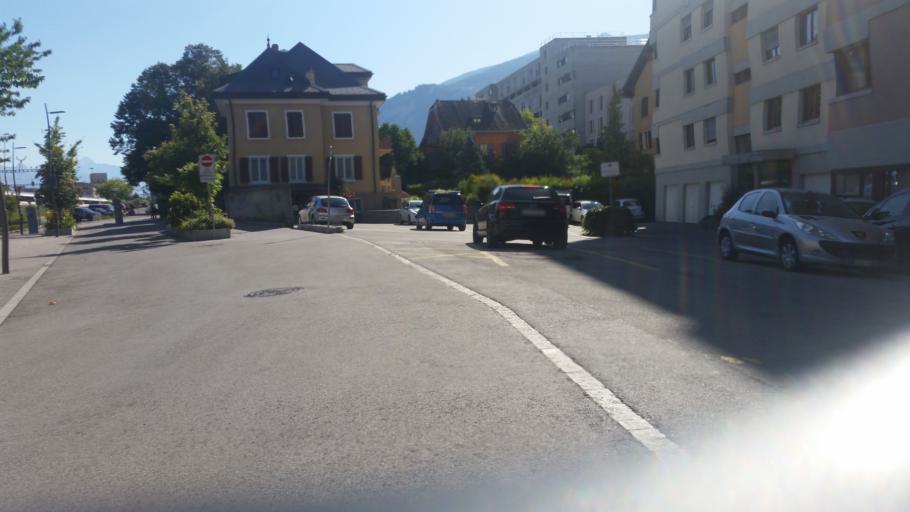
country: CH
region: Valais
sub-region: Sion District
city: Sitten
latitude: 46.2263
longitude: 7.3570
